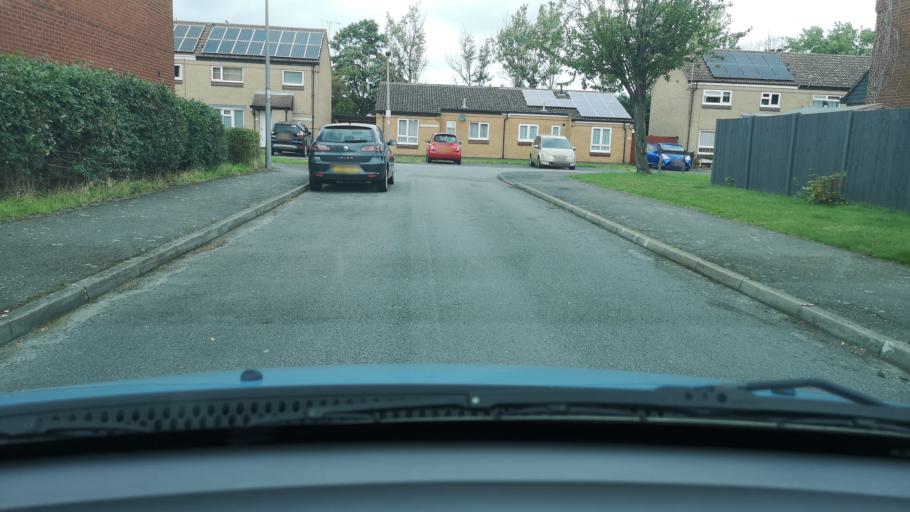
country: GB
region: England
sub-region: North Lincolnshire
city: Gunness
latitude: 53.5884
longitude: -0.6908
